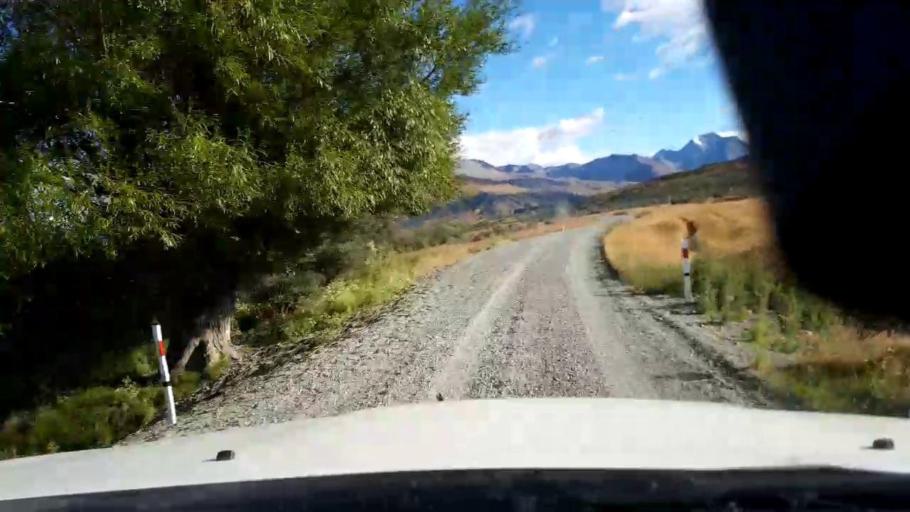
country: NZ
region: Canterbury
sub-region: Timaru District
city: Pleasant Point
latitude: -43.7498
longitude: 170.5711
